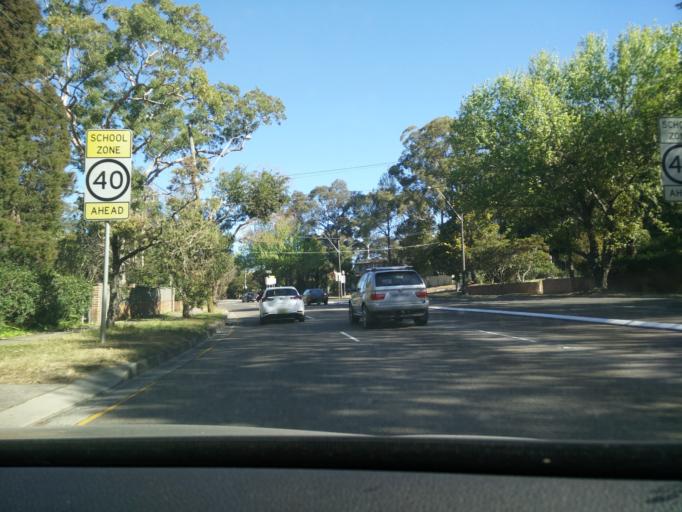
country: AU
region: New South Wales
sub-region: City of Sydney
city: Pymble
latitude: -33.7570
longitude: 151.1377
